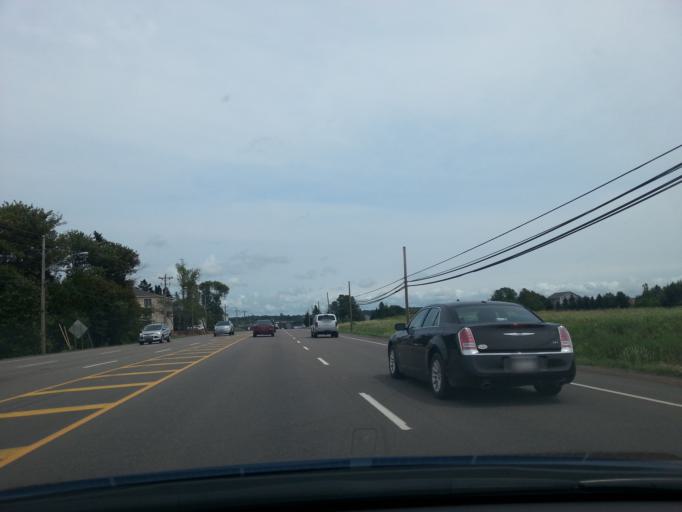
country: CA
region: Prince Edward Island
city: Charlottetown
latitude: 46.2618
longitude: -63.1679
